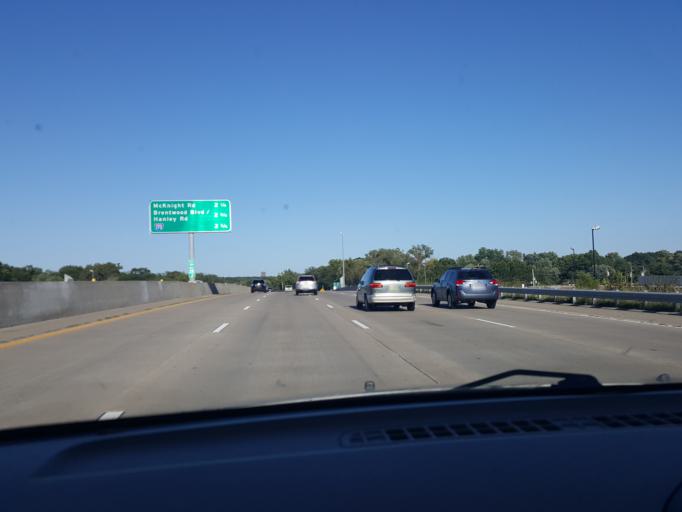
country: US
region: Missouri
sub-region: Saint Louis County
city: Frontenac
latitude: 38.6355
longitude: -90.4072
